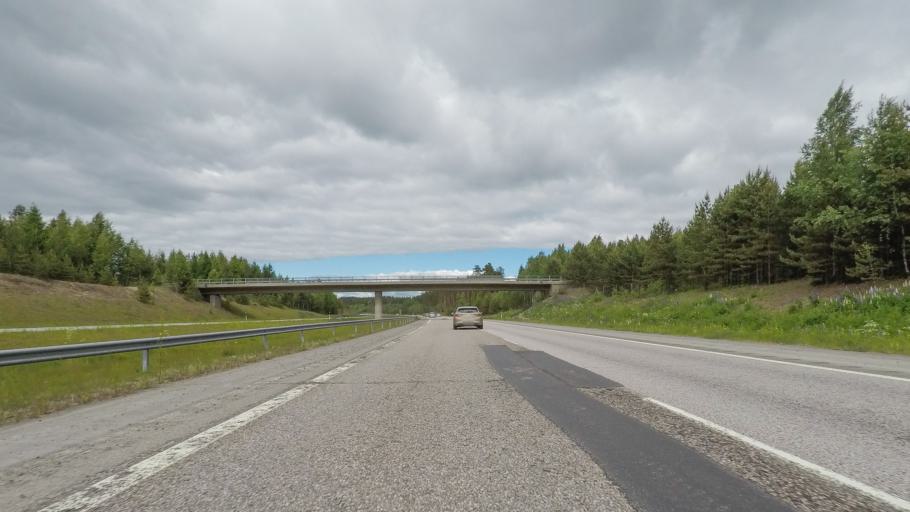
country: FI
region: Paijanne Tavastia
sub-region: Lahti
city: Heinola
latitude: 61.1641
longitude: 25.9972
